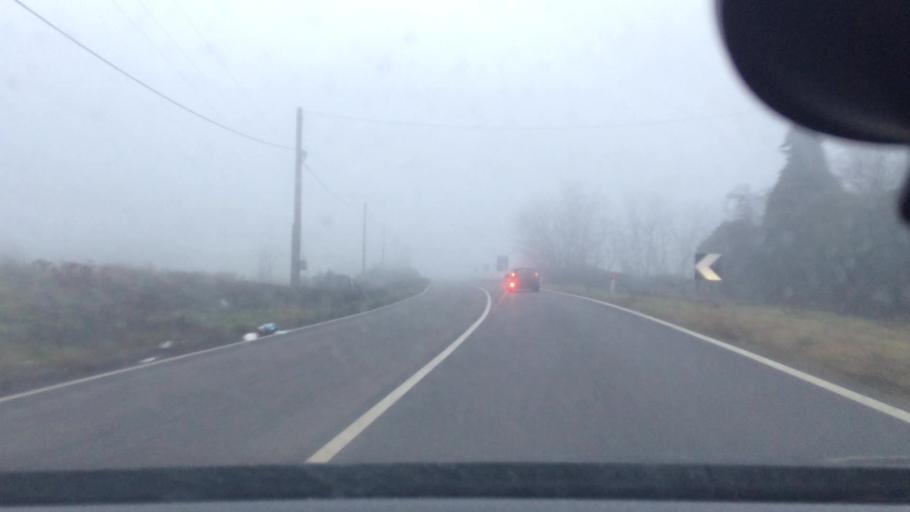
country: IT
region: Lombardy
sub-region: Citta metropolitana di Milano
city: Cantalupo
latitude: 45.5691
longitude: 8.9950
